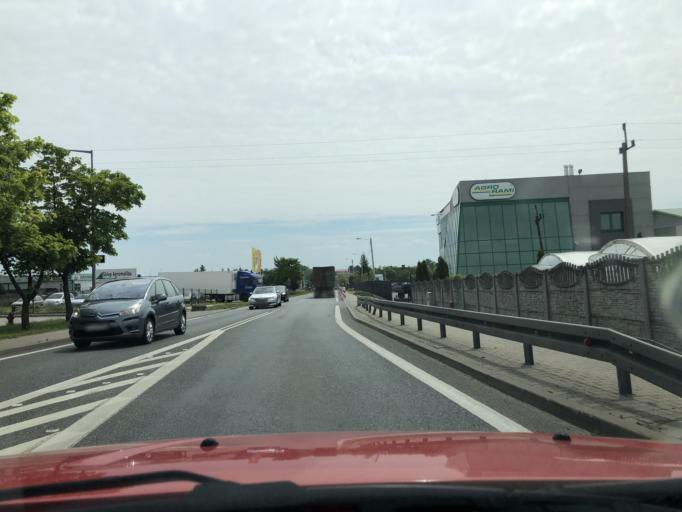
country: PL
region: Greater Poland Voivodeship
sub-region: Powiat ostrowski
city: Nowe Skalmierzyce
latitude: 51.7892
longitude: 18.0030
